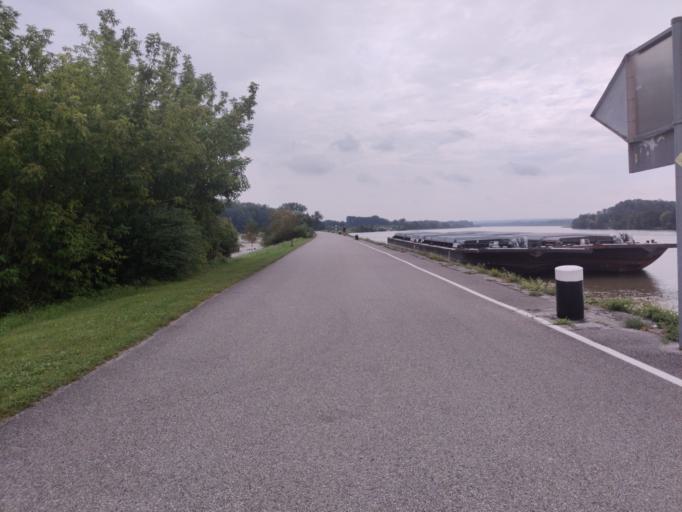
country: AT
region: Upper Austria
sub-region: Politischer Bezirk Perg
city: Perg
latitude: 48.2247
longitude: 14.5849
